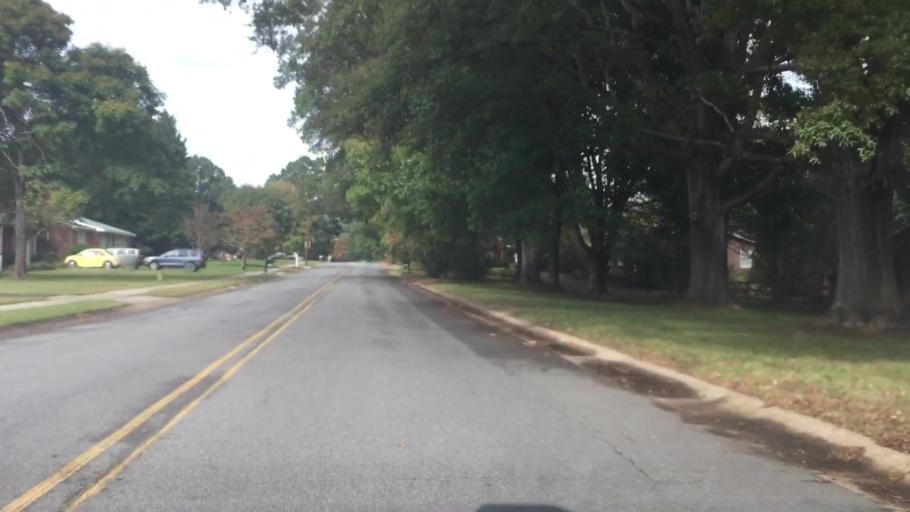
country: US
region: North Carolina
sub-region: Iredell County
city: Mooresville
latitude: 35.5654
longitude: -80.8003
